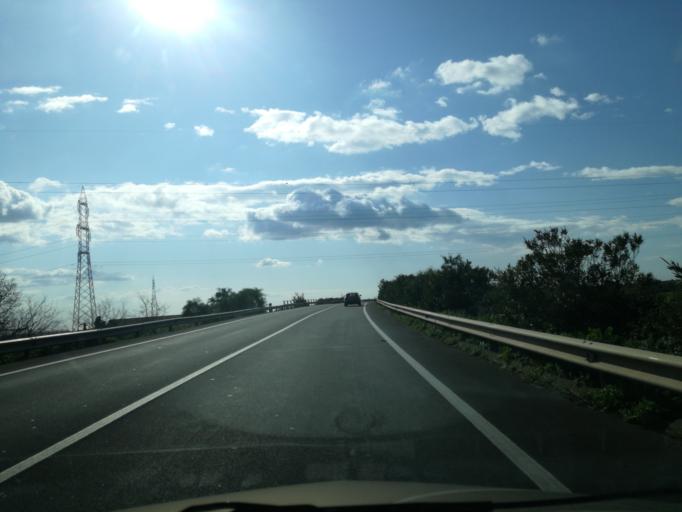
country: IT
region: Sicily
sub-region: Ragusa
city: Ragusa
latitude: 36.8844
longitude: 14.6995
